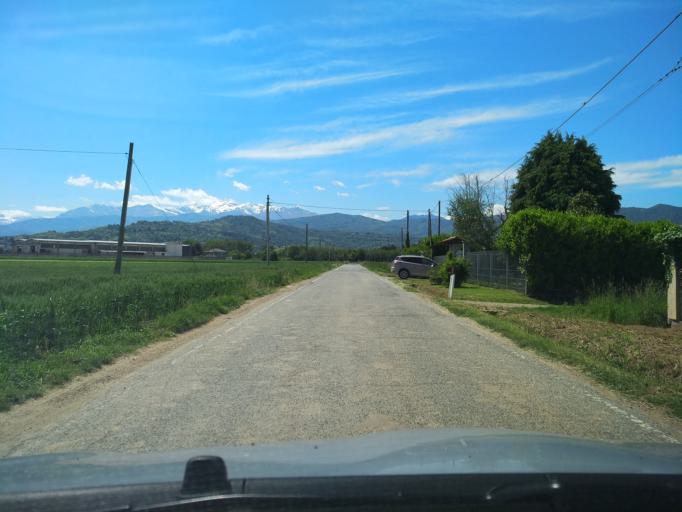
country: IT
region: Piedmont
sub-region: Provincia di Torino
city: Frossasco
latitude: 44.9102
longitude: 7.3727
